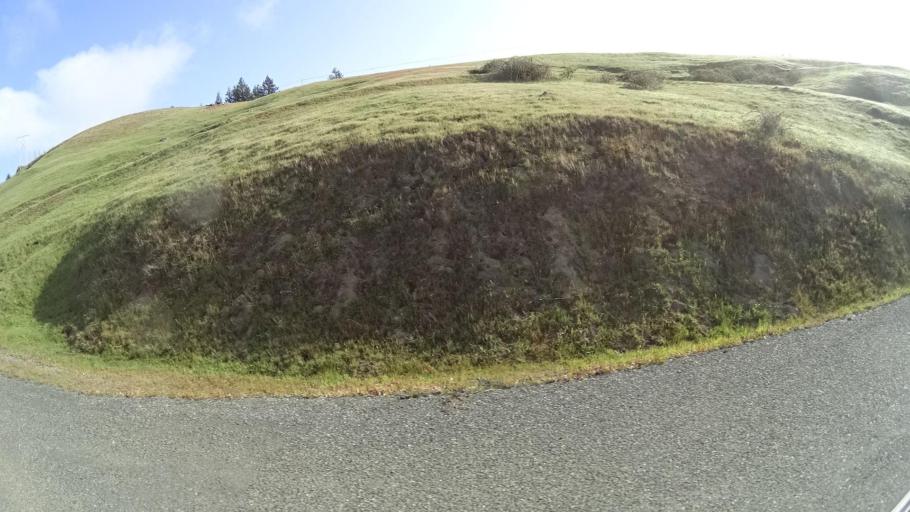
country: US
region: California
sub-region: Humboldt County
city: Blue Lake
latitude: 40.7199
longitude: -123.9439
